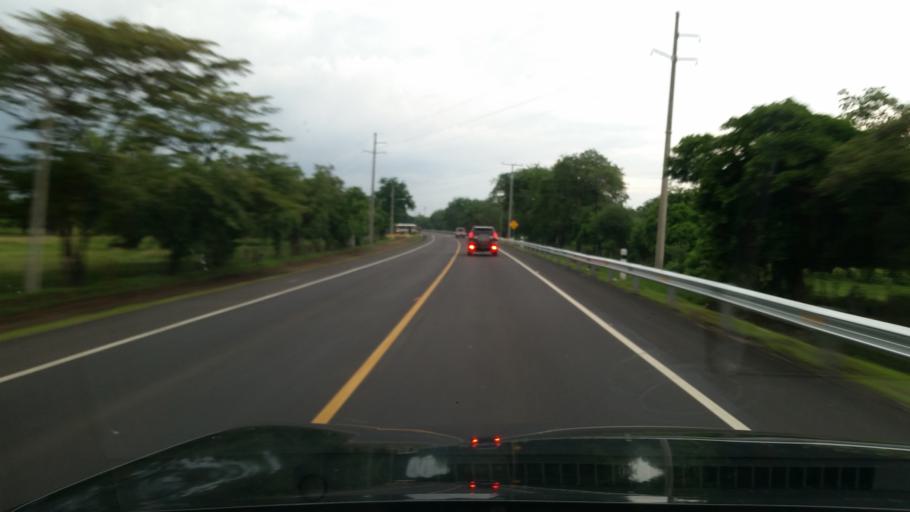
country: NI
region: Leon
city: Nagarote
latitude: 12.2778
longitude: -86.5768
